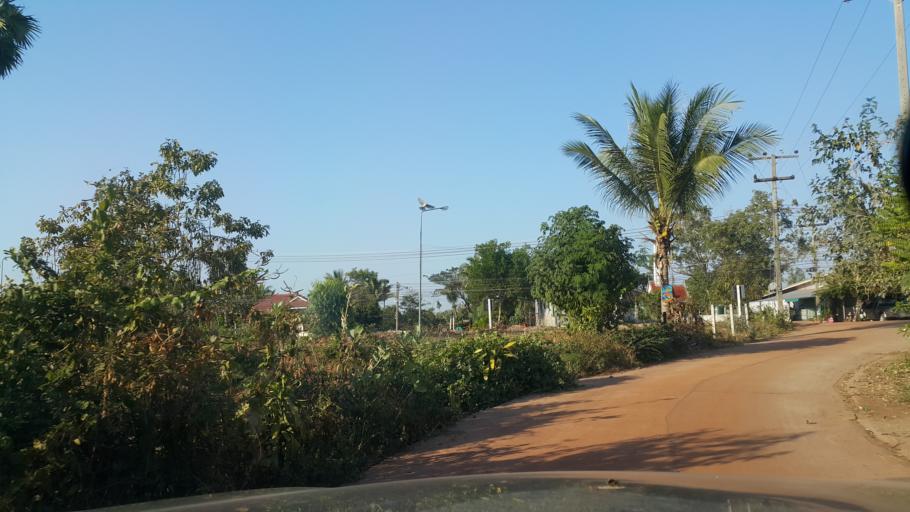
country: TH
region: Changwat Udon Thani
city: Ban Na Muang
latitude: 17.2316
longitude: 103.0434
